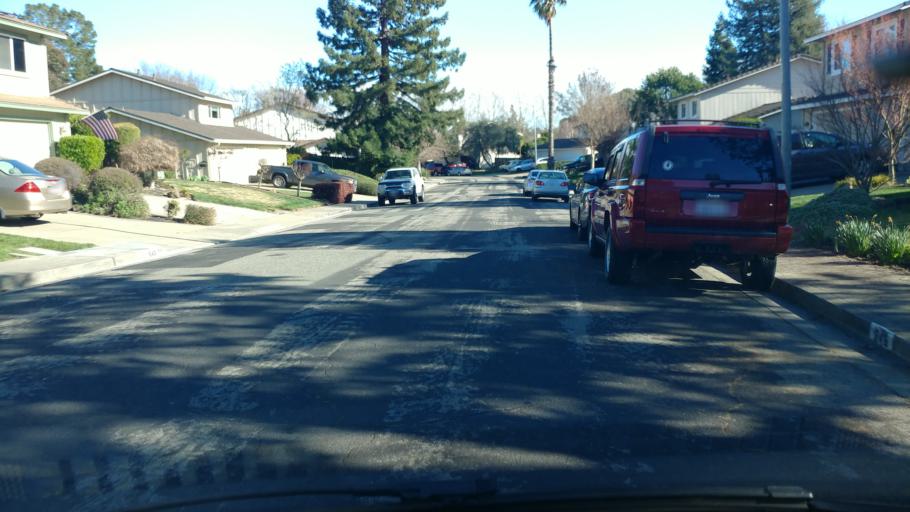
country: US
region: California
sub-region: Contra Costa County
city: San Ramon
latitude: 37.7701
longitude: -121.9886
